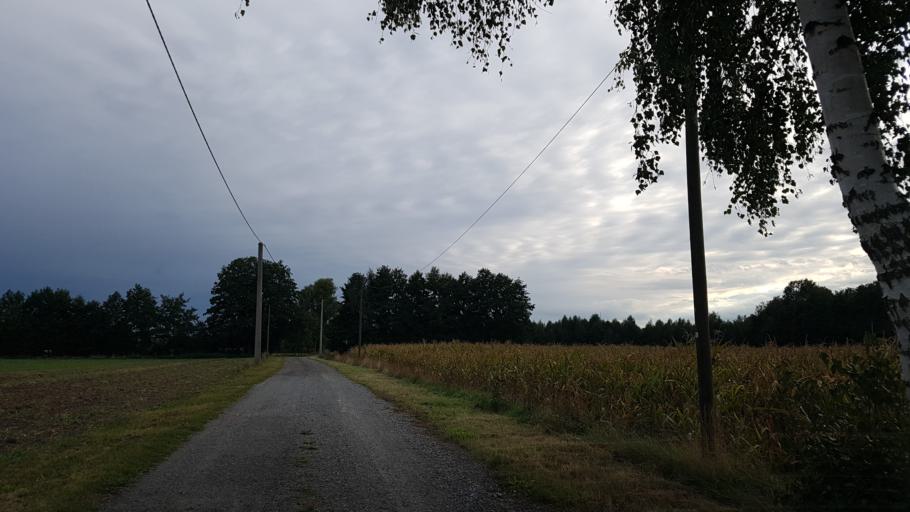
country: DE
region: Brandenburg
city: Bad Liebenwerda
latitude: 51.5287
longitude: 13.4385
